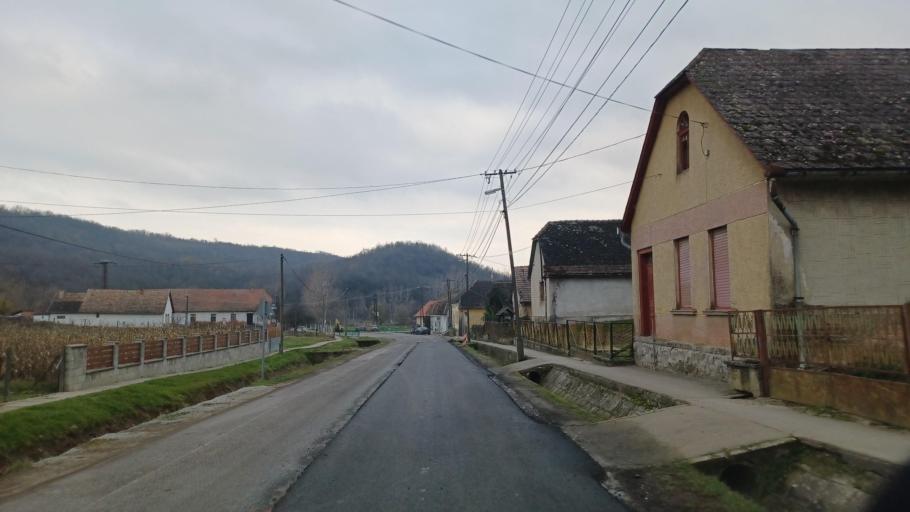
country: HU
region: Tolna
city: Zomba
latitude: 46.5012
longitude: 18.5649
